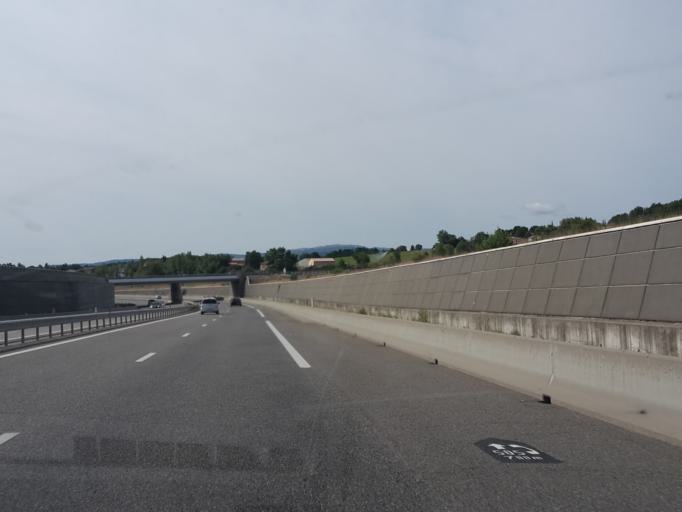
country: FR
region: Provence-Alpes-Cote d'Azur
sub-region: Departement des Hautes-Alpes
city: Laragne-Monteglin
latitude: 44.3229
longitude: 5.8923
